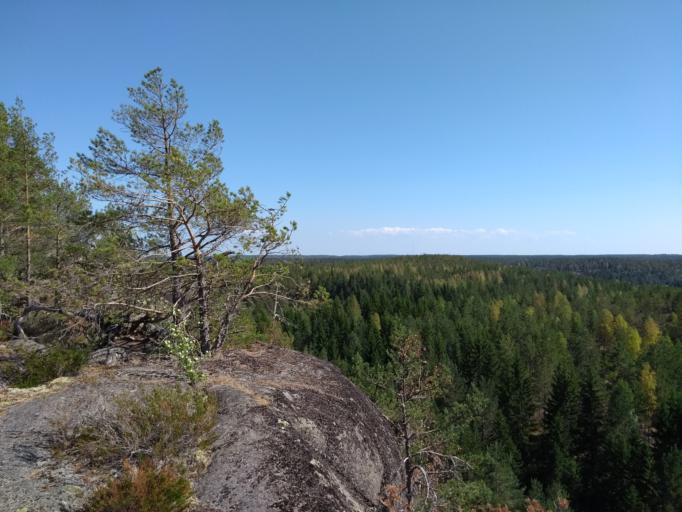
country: SE
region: OEstergoetland
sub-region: Norrkopings Kommun
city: Krokek
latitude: 58.7570
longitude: 16.3640
